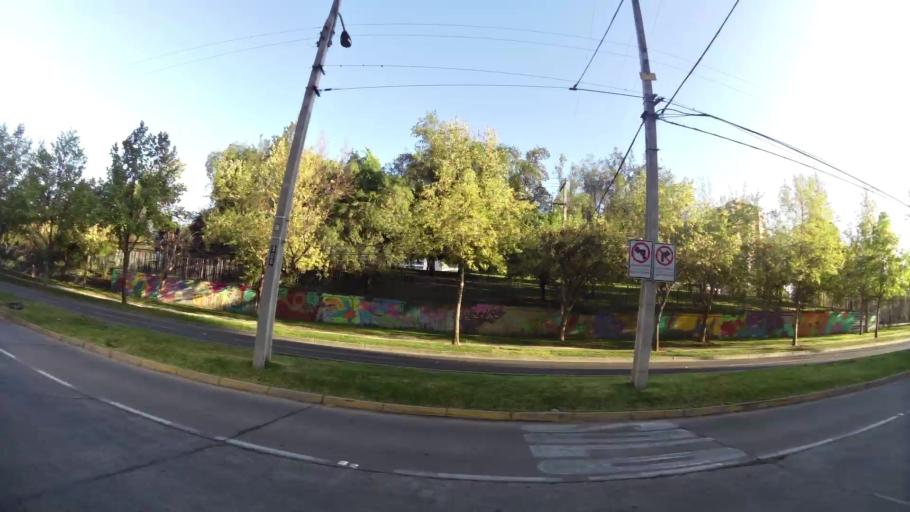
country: CL
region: Santiago Metropolitan
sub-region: Provincia de Santiago
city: Villa Presidente Frei, Nunoa, Santiago, Chile
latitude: -33.4026
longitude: -70.5704
